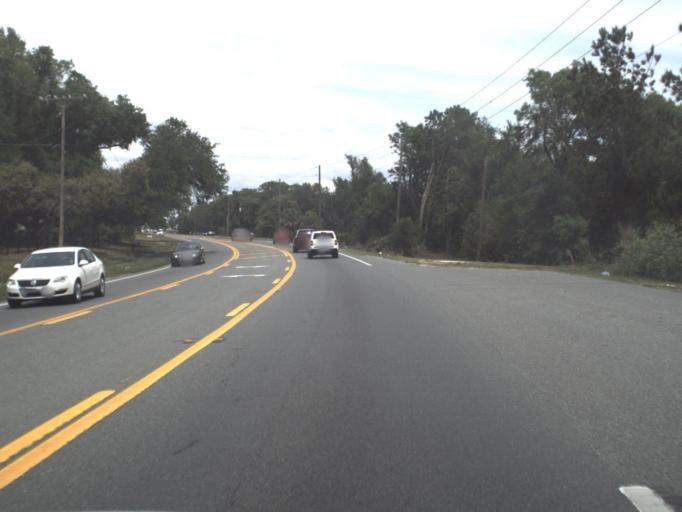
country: US
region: Florida
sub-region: Lake County
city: Mount Dora
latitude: 28.8407
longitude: -81.6339
